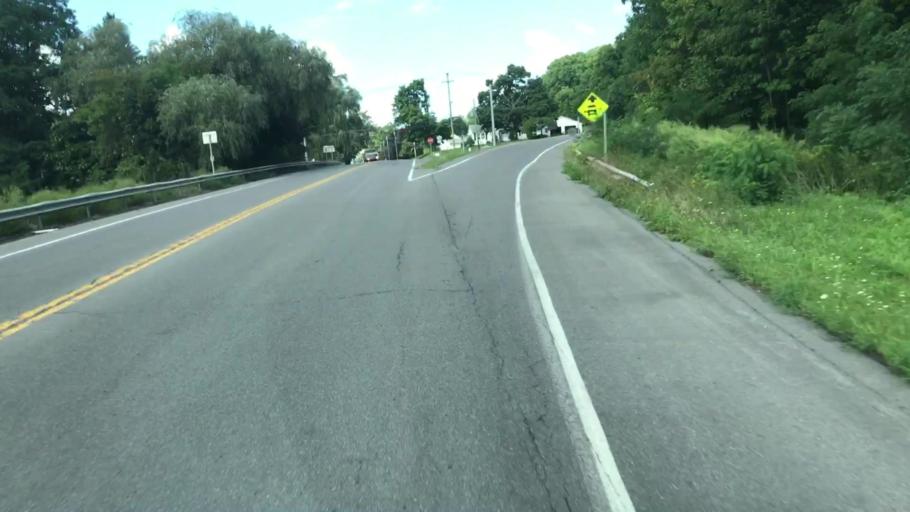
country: US
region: New York
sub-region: Onondaga County
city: Marcellus
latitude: 42.9815
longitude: -76.3313
